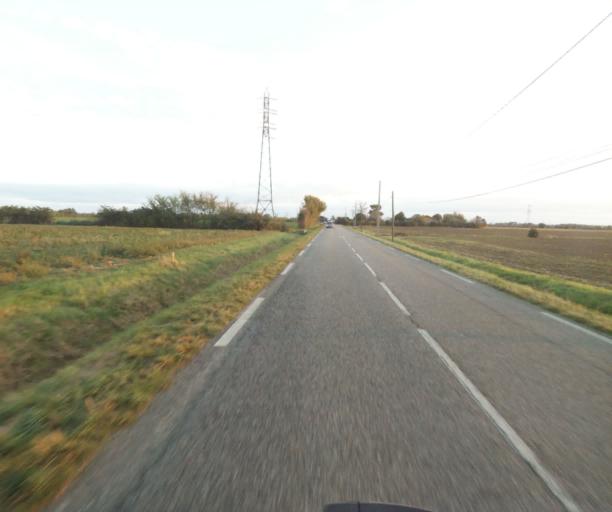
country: FR
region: Midi-Pyrenees
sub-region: Departement du Tarn-et-Garonne
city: Verdun-sur-Garonne
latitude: 43.8373
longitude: 1.2397
